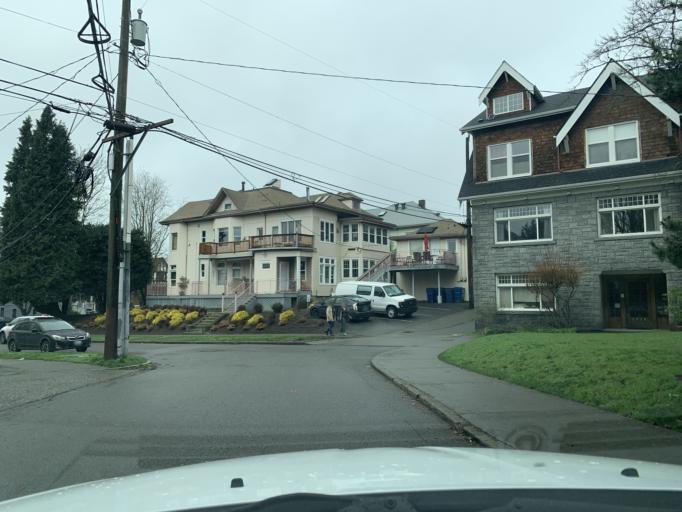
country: US
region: Washington
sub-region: King County
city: Seattle
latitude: 47.6187
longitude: -122.3134
